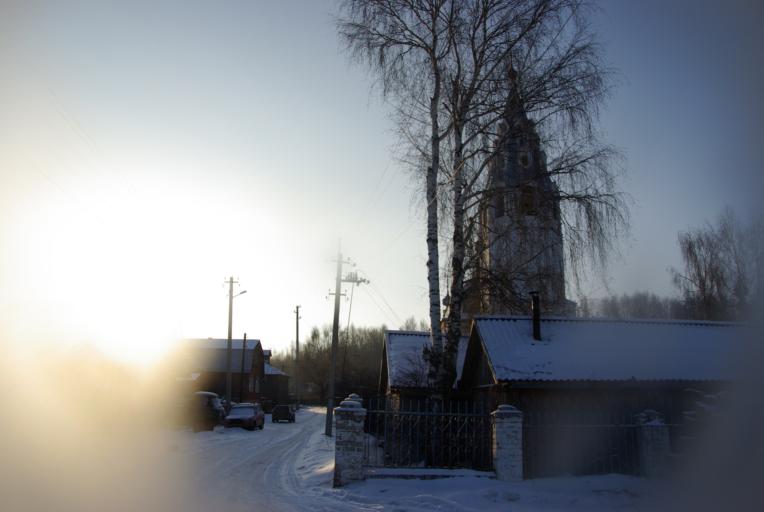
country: RU
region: Kostroma
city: Galich
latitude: 58.3933
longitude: 42.3635
